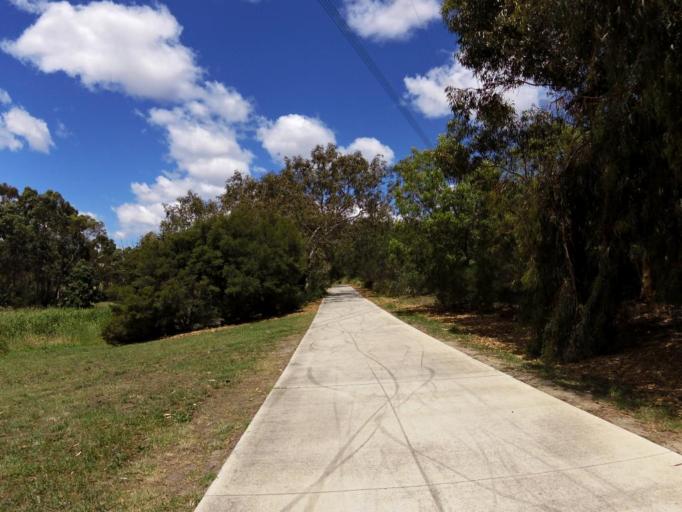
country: AU
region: Victoria
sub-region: Hume
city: Jacana
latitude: -37.6829
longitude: 144.9027
